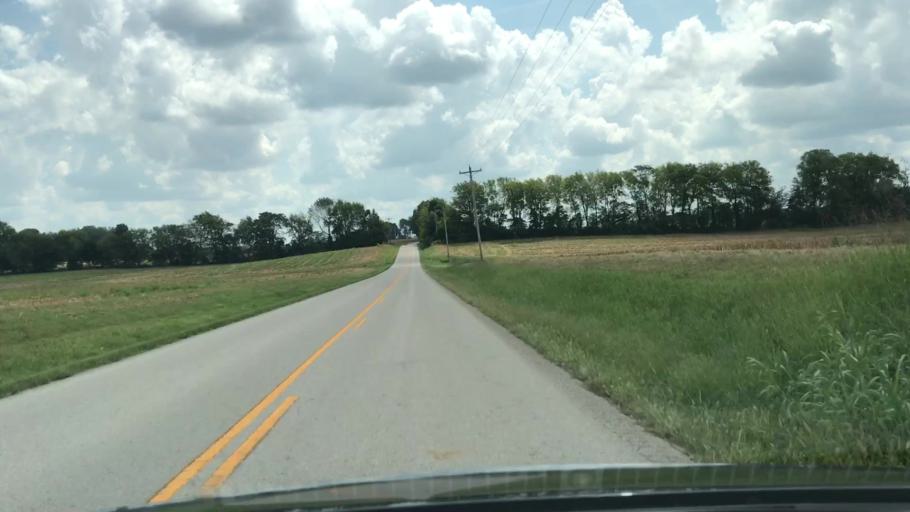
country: US
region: Kentucky
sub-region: Todd County
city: Elkton
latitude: 36.7844
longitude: -87.1277
